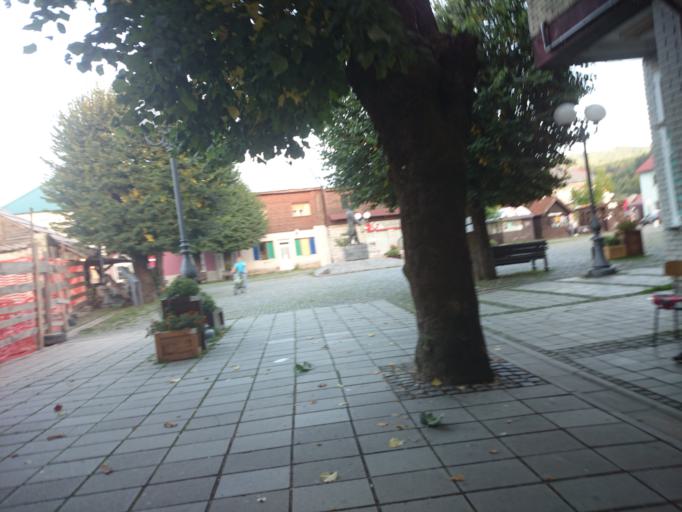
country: ME
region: Opstina Kolasin
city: Kolasin
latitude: 42.8238
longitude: 19.5224
